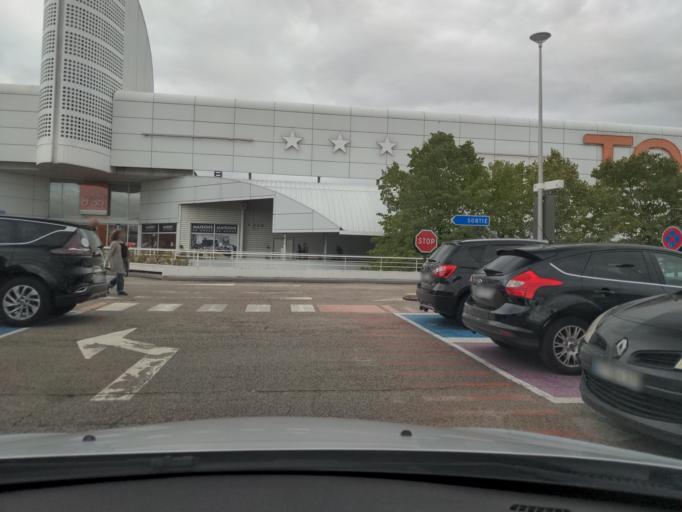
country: FR
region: Bourgogne
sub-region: Departement de la Cote-d'Or
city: Ahuy
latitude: 47.3573
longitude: 5.0500
